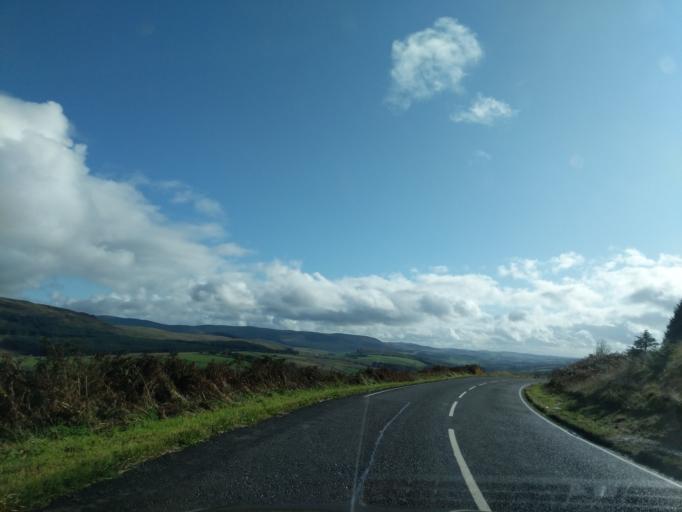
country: GB
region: Scotland
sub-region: Dumfries and Galloway
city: Moffat
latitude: 55.3765
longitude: -3.4776
